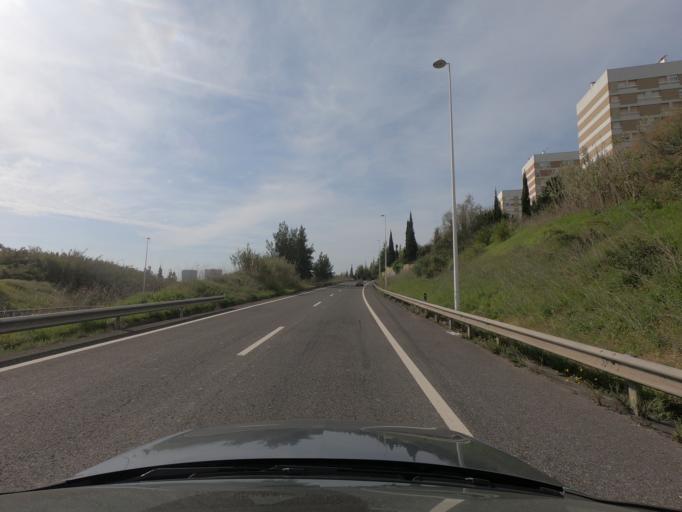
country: PT
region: Lisbon
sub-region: Loures
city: Moscavide
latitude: 38.7837
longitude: -9.1067
